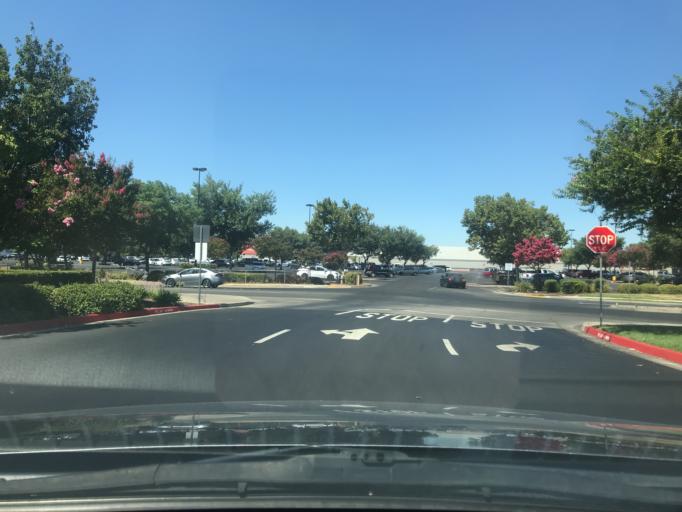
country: US
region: California
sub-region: Merced County
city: Merced
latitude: 37.3182
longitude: -120.4993
